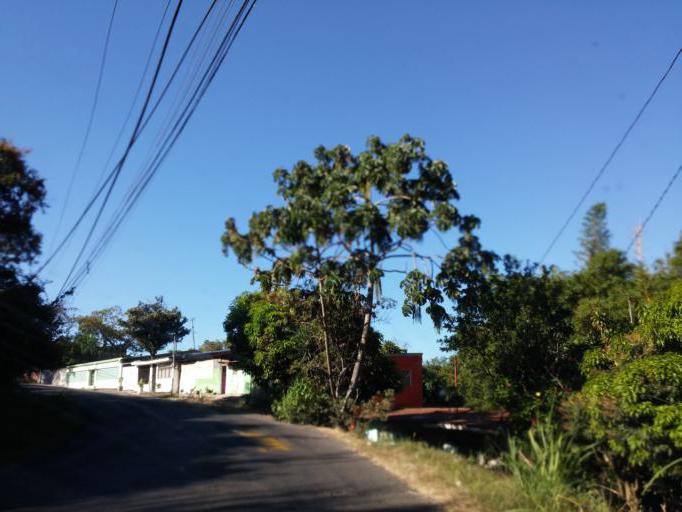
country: CR
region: Alajuela
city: Sabanilla
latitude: 10.0497
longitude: -84.2147
